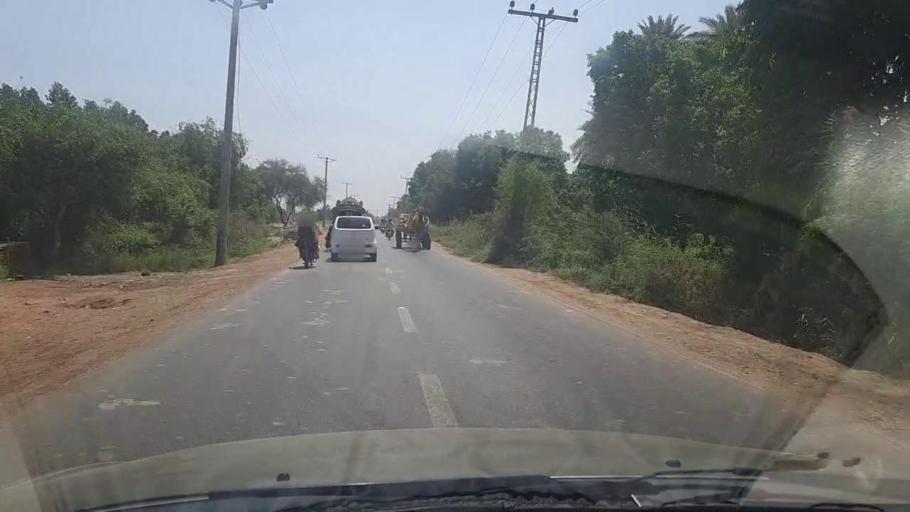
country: PK
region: Sindh
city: Hyderabad
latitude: 25.3910
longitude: 68.4078
